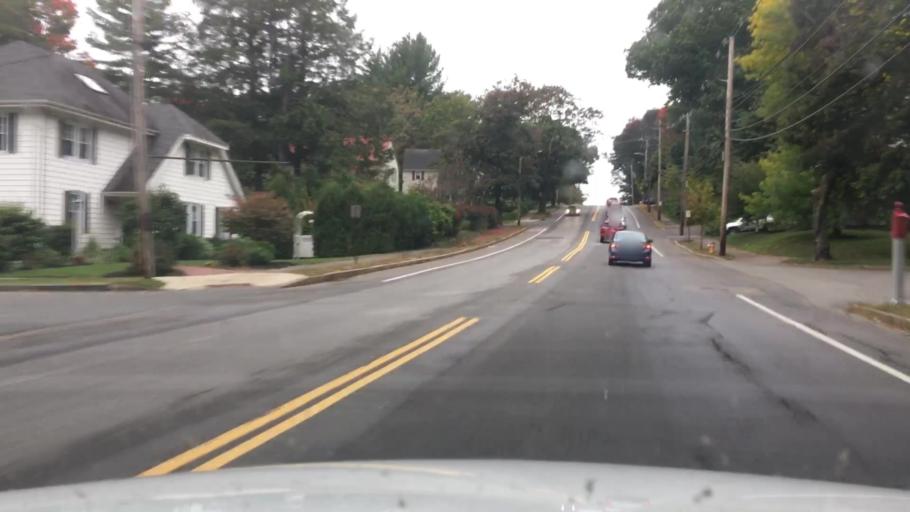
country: US
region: Maine
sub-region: Cumberland County
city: Portland
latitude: 43.6646
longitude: -70.2884
